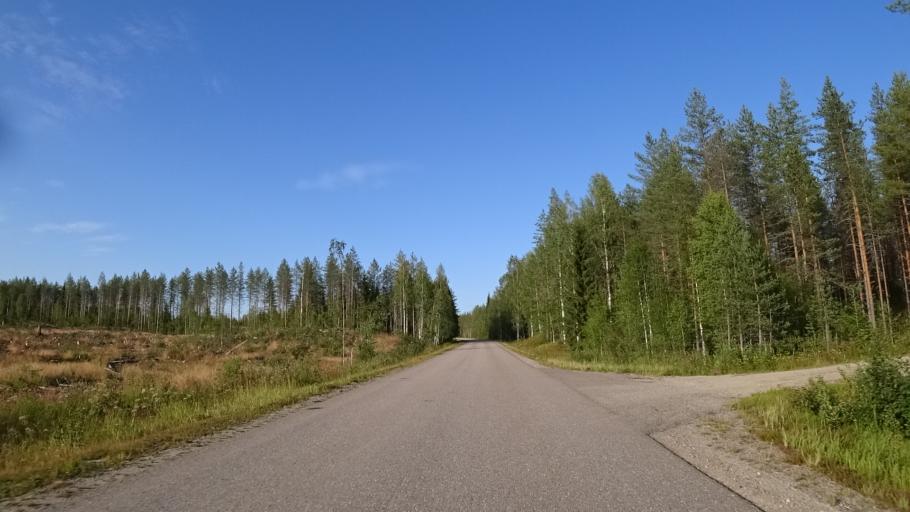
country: FI
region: North Karelia
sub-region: Joensuu
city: Eno
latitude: 63.0307
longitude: 30.5264
